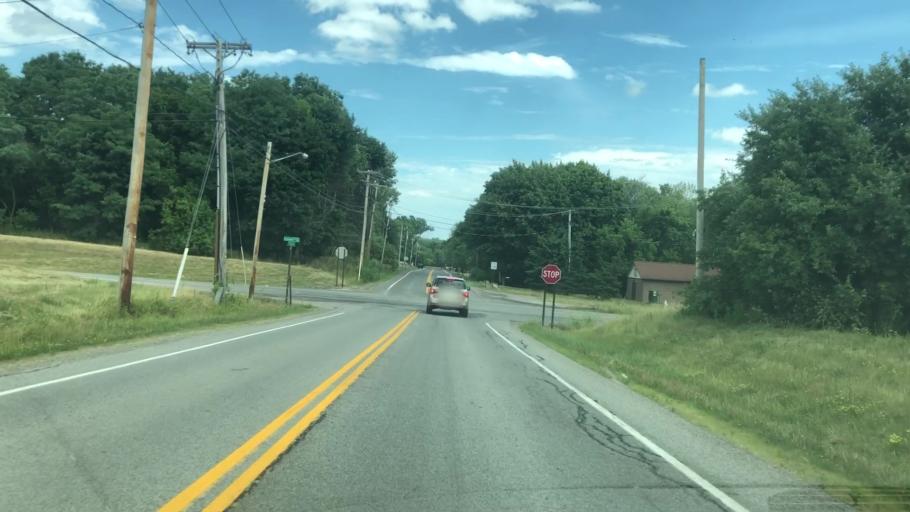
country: US
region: New York
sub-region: Wayne County
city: Macedon
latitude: 43.1276
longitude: -77.3533
